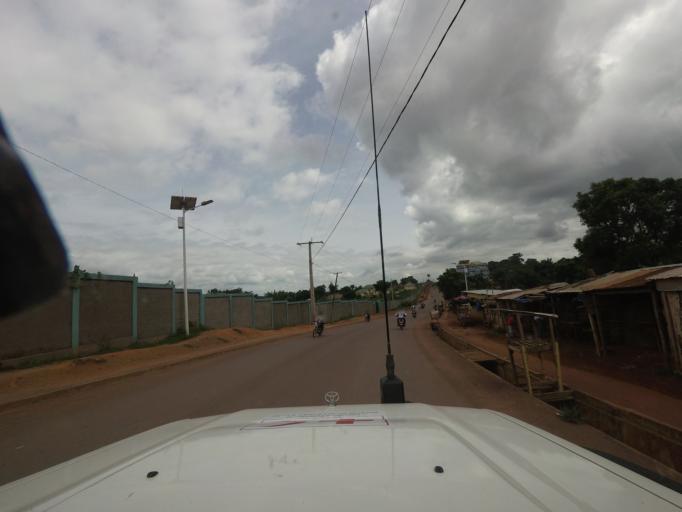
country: GN
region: Nzerekore
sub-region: Nzerekore Prefecture
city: Nzerekore
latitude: 7.7446
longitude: -8.8219
